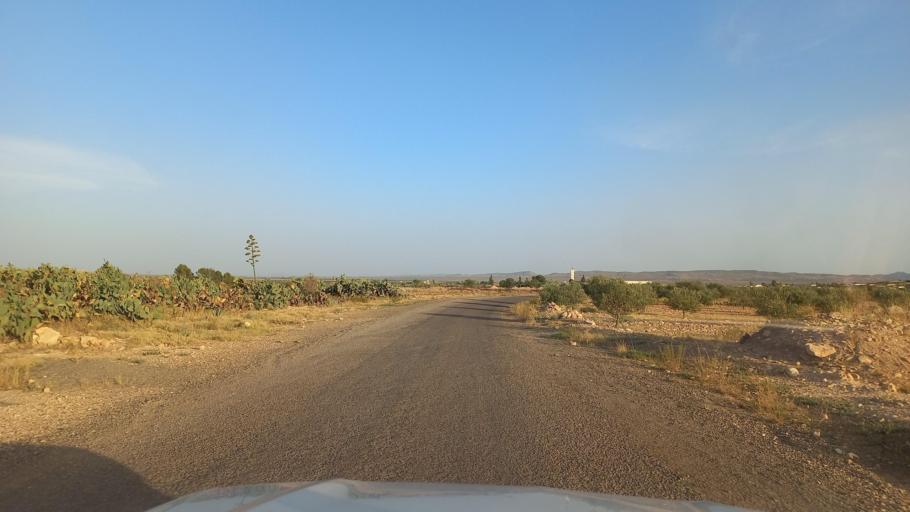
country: TN
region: Al Qasrayn
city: Kasserine
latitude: 35.2691
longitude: 8.9312
